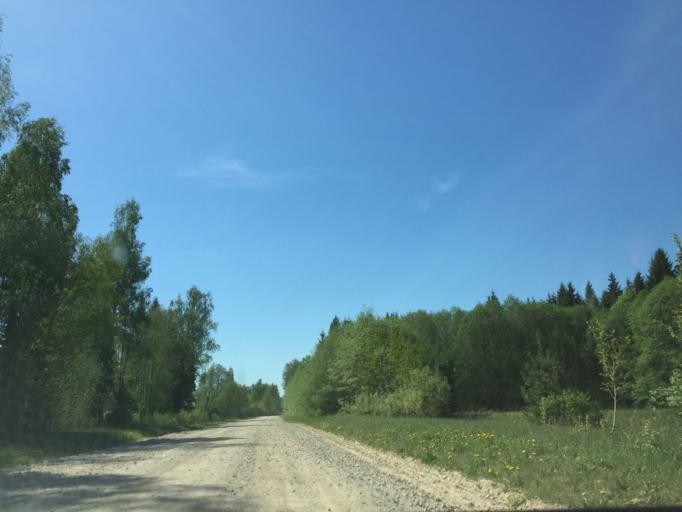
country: LV
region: Kegums
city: Kegums
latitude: 56.8855
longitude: 24.7887
